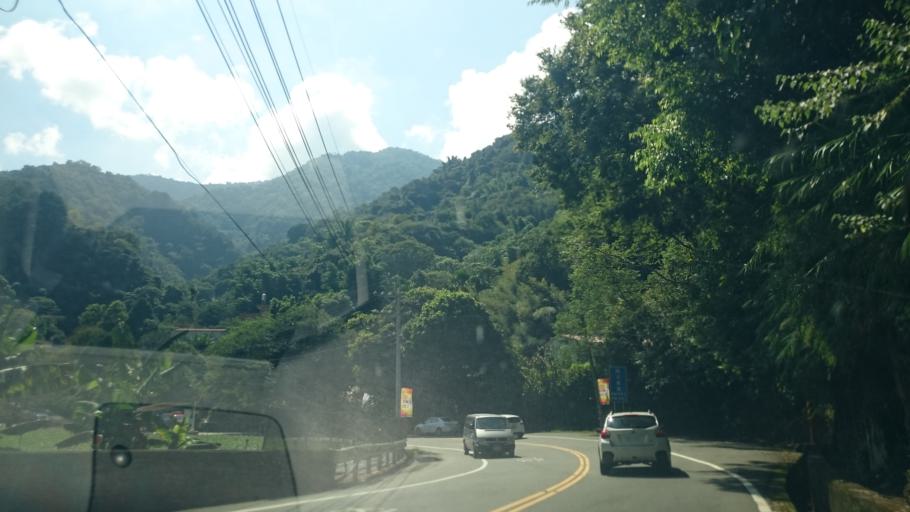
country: TW
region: Taiwan
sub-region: Nantou
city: Puli
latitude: 23.9953
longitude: 121.0761
